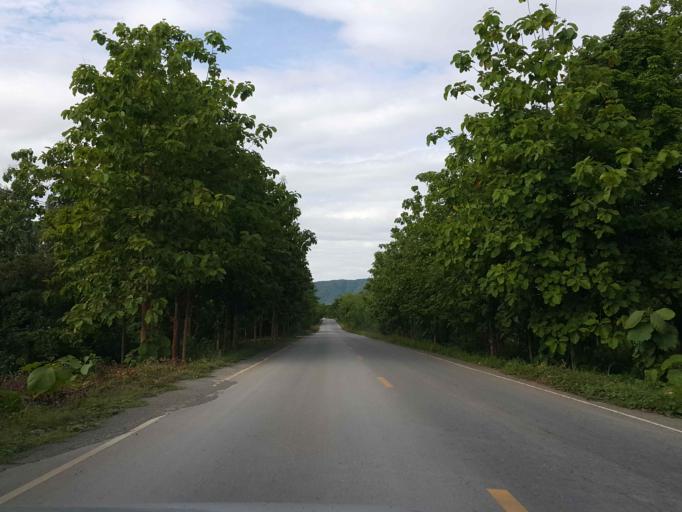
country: TH
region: Sukhothai
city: Thung Saliam
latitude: 17.2485
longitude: 99.5184
